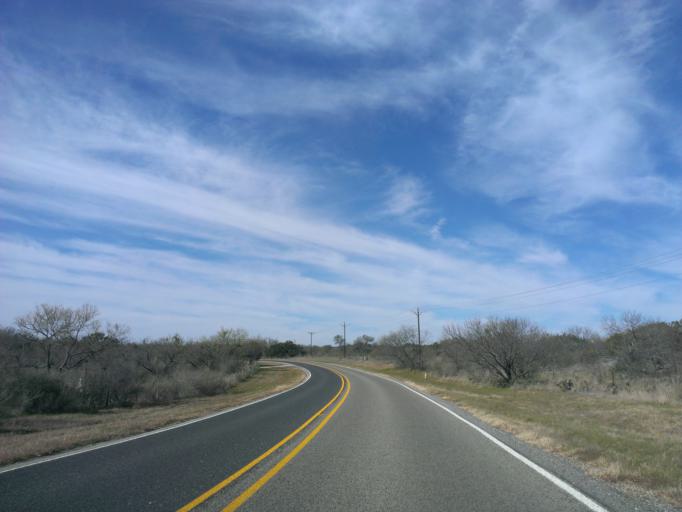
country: US
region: Texas
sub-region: Burnet County
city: Granite Shoals
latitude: 30.5953
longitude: -98.4308
